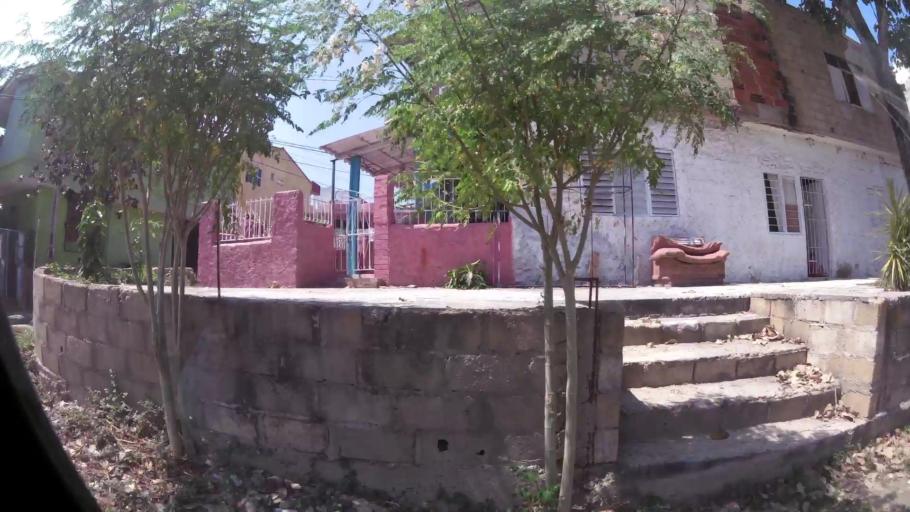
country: CO
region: Bolivar
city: Cartagena
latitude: 10.4027
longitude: -75.4887
